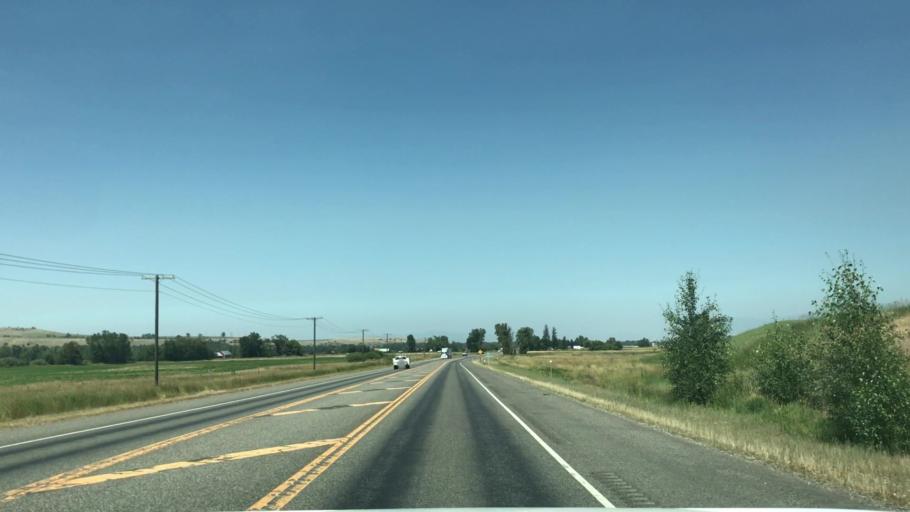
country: US
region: Montana
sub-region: Gallatin County
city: Four Corners
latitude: 45.6149
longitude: -111.1966
